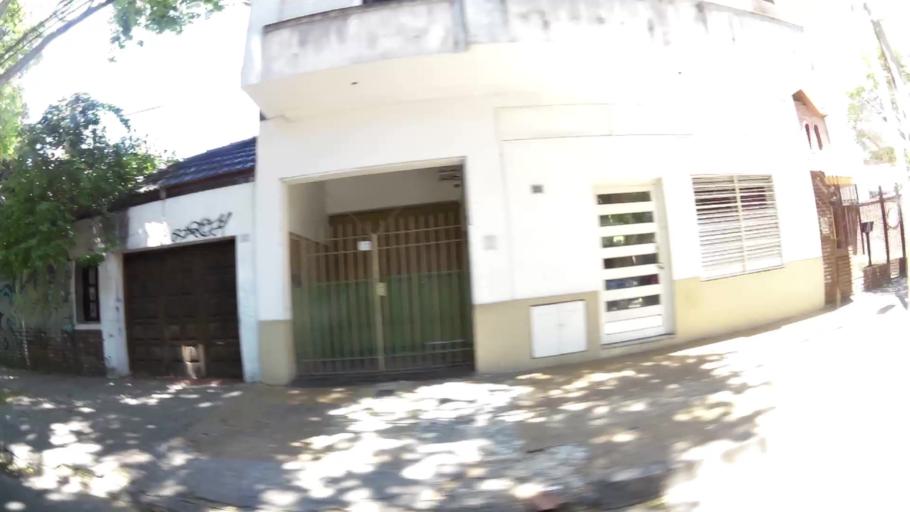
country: AR
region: Buenos Aires
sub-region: Partido de General San Martin
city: General San Martin
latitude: -34.5780
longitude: -58.5335
